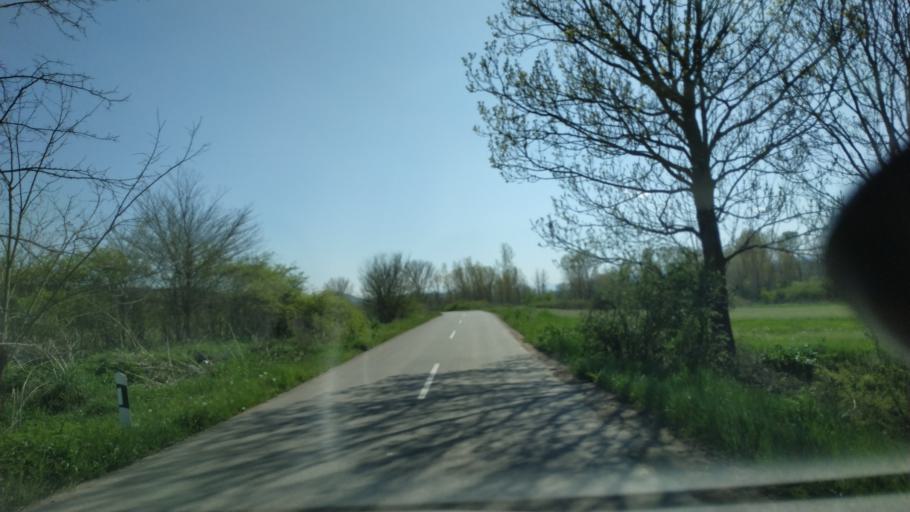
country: RS
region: Central Serbia
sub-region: Nisavski Okrug
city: Nis
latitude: 43.4738
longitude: 21.8659
